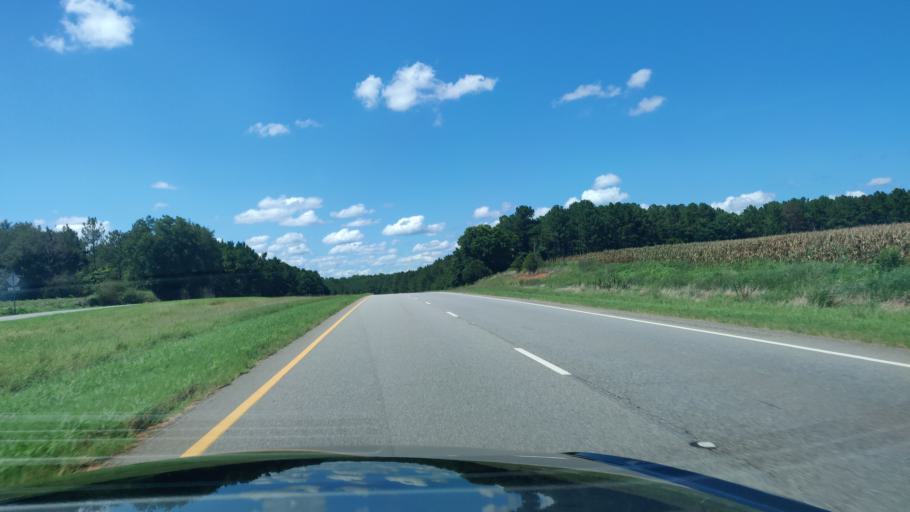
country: US
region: Georgia
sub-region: Terrell County
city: Dawson
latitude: 31.8620
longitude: -84.4831
